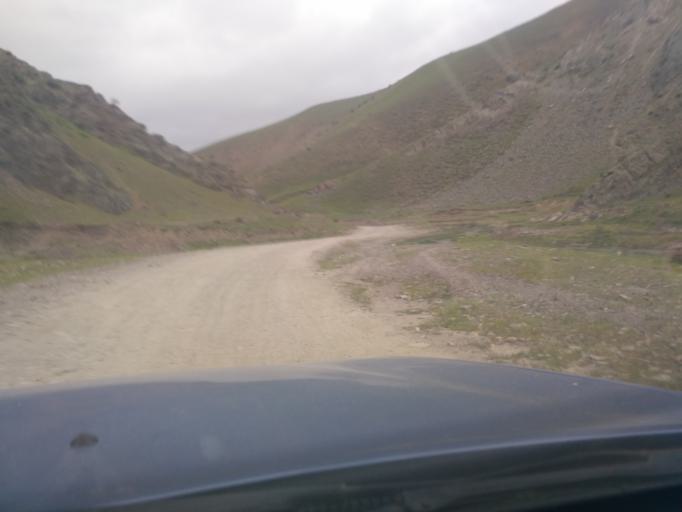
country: UZ
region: Jizzax
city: Zomin
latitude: 39.8518
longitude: 68.3957
